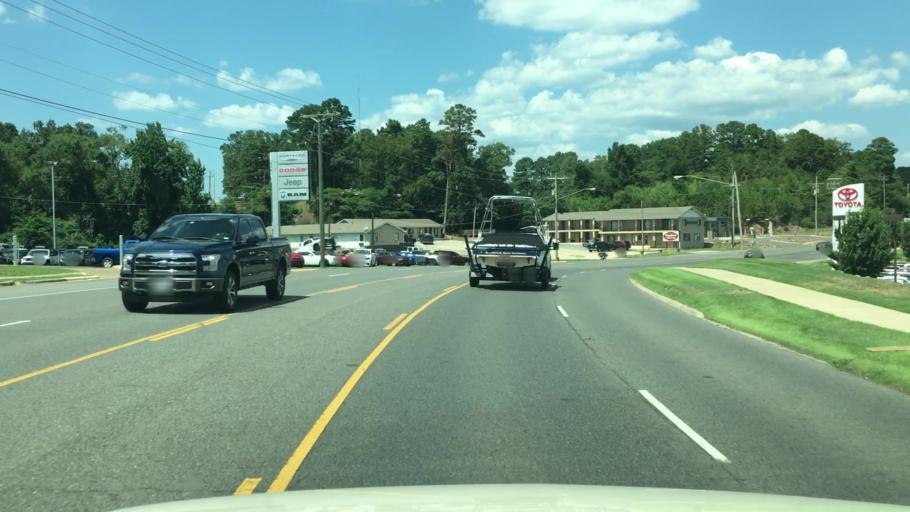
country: US
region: Arkansas
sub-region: Garland County
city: Lake Hamilton
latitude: 34.4457
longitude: -93.0900
